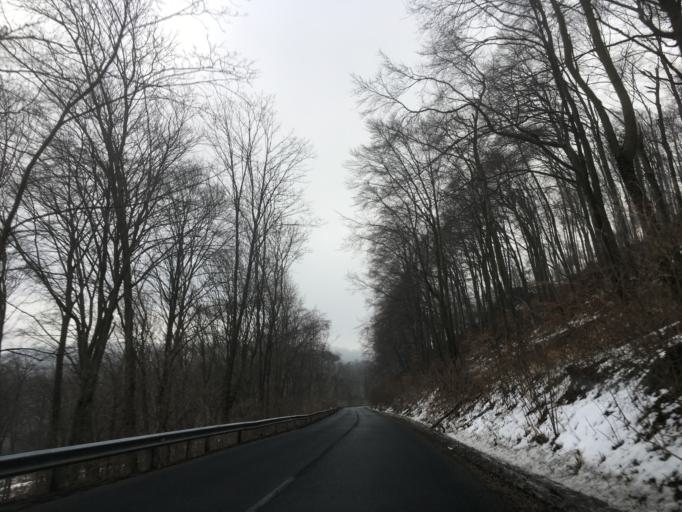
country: HU
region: Komarom-Esztergom
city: Kesztolc
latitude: 47.7208
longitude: 18.8539
